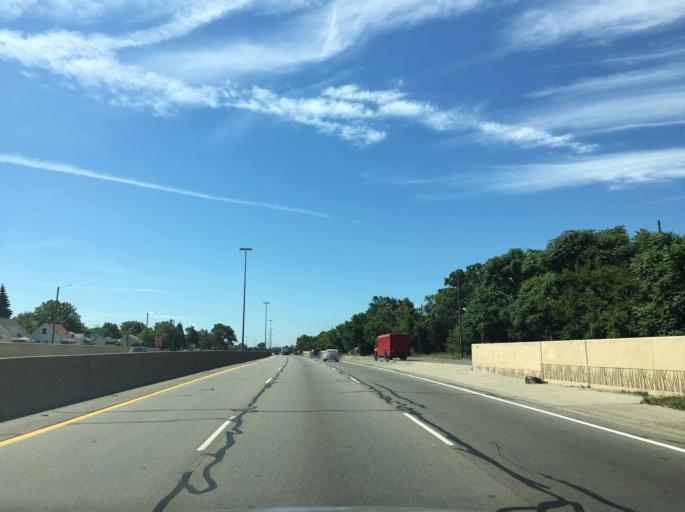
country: US
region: Michigan
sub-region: Wayne County
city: Dearborn
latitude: 42.3416
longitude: -83.2163
